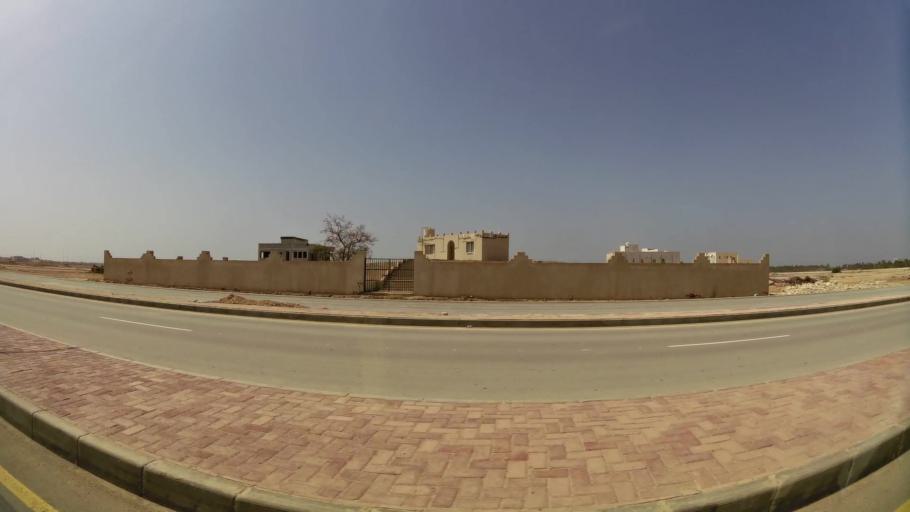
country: OM
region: Zufar
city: Salalah
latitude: 17.0399
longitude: 54.1237
